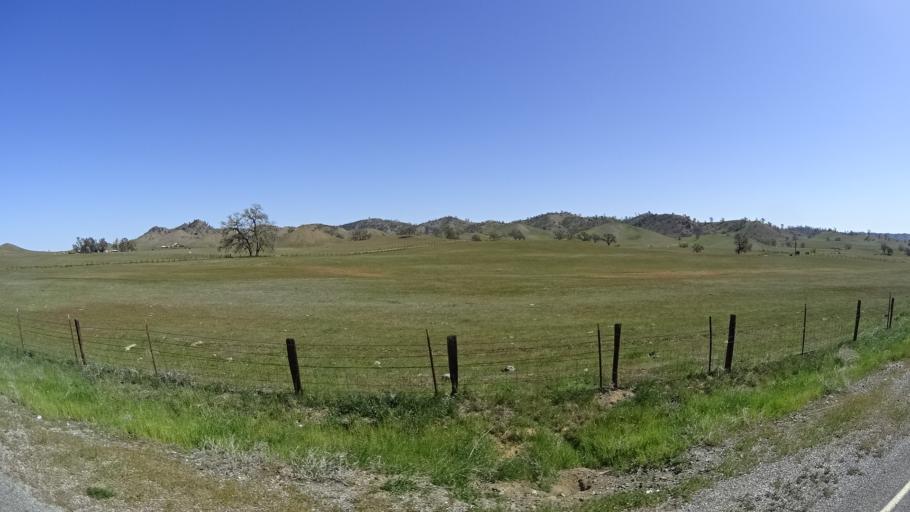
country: US
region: California
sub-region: Glenn County
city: Orland
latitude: 39.6886
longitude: -122.5447
